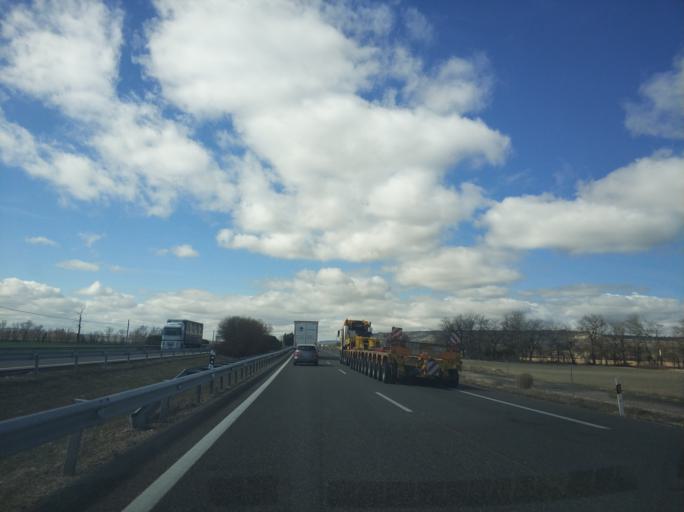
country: ES
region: Castille and Leon
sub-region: Provincia de Palencia
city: Villodrigo
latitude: 42.1354
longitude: -4.1160
